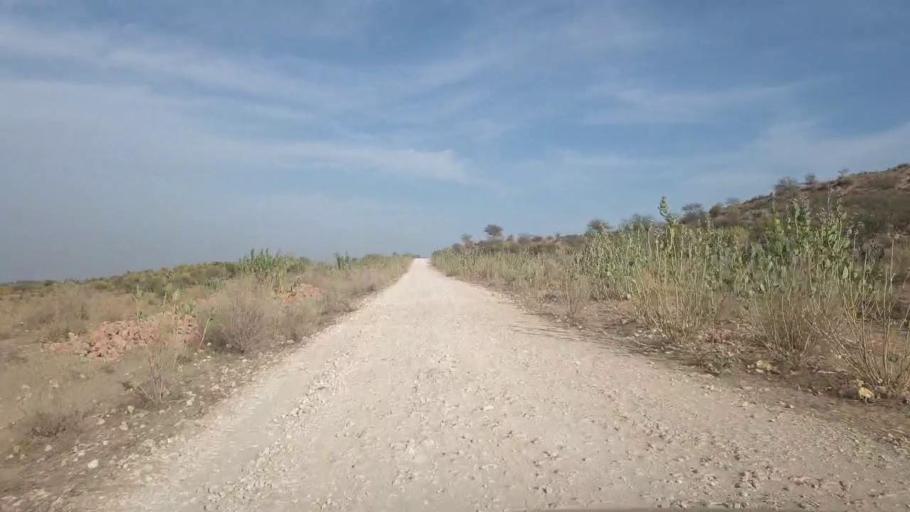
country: PK
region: Sindh
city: Nabisar
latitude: 25.0525
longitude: 69.7119
